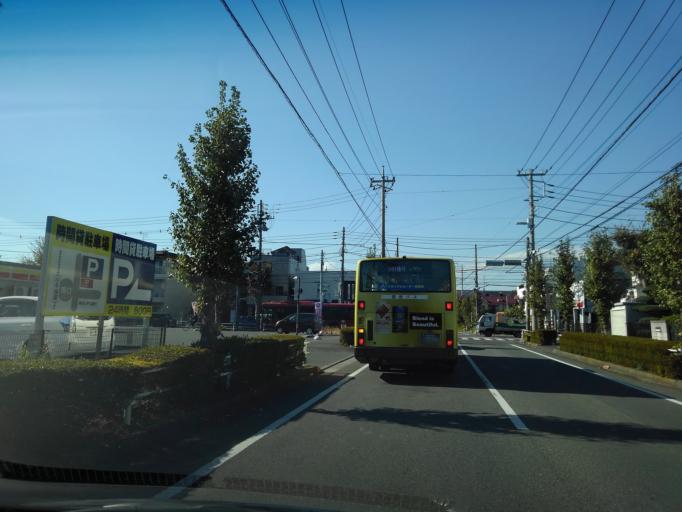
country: JP
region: Saitama
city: Tokorozawa
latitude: 35.7995
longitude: 139.4339
